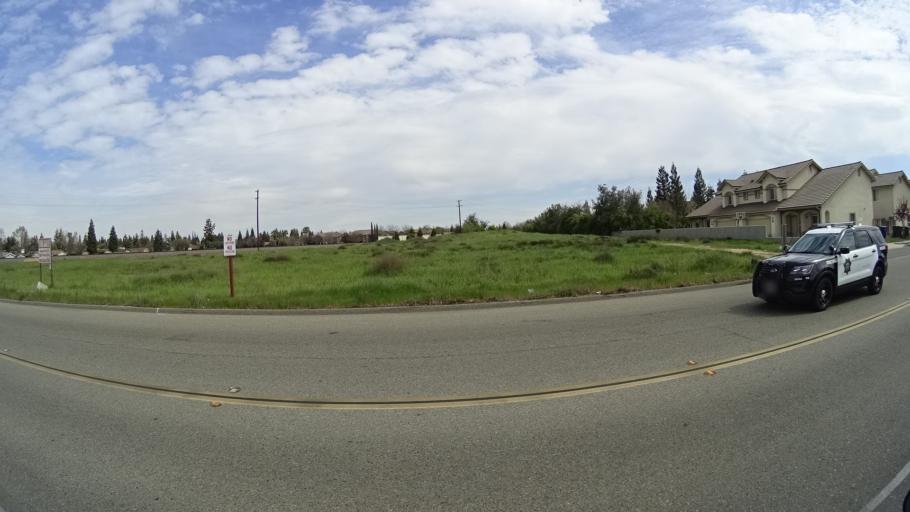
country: US
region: California
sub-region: Fresno County
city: West Park
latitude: 36.8281
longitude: -119.8746
